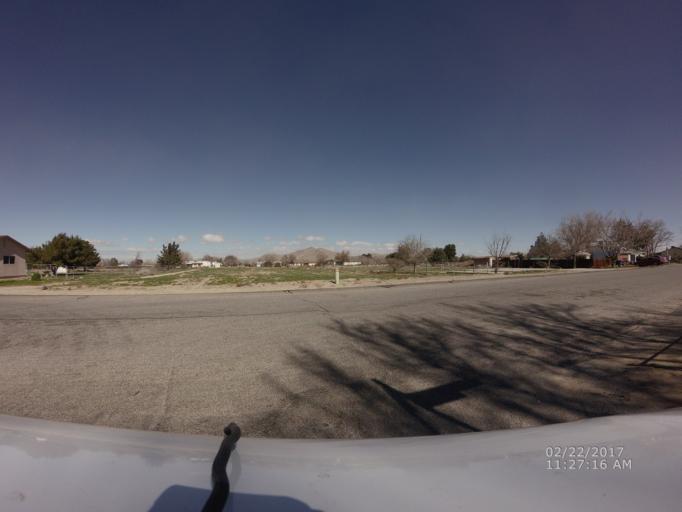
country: US
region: California
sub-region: Los Angeles County
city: Lake Los Angeles
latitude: 34.6230
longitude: -117.8149
